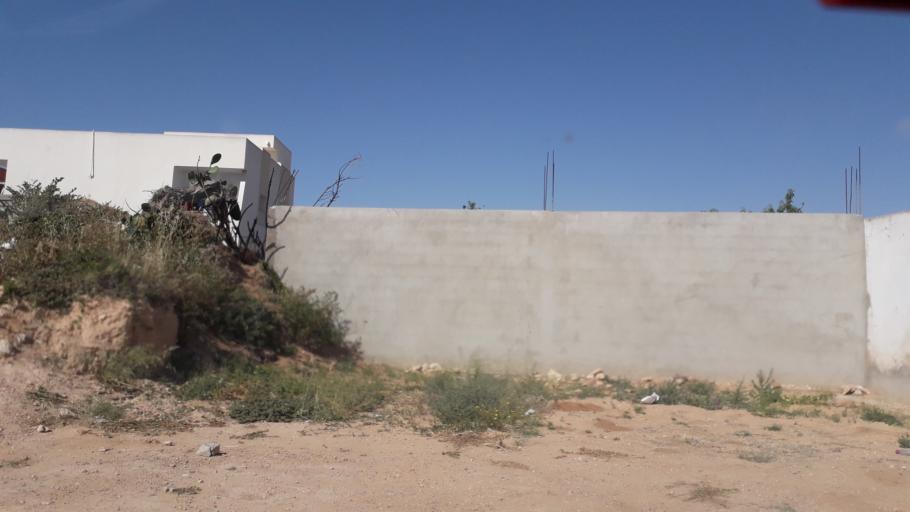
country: TN
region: Safaqis
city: Al Qarmadah
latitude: 34.8071
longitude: 10.7631
